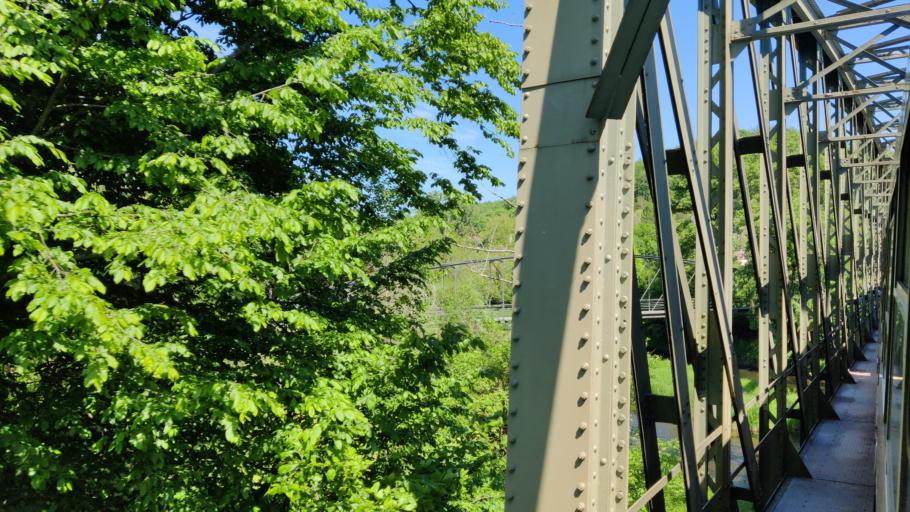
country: AT
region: Lower Austria
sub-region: Politischer Bezirk Horn
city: Horn
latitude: 48.6263
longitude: 15.6420
